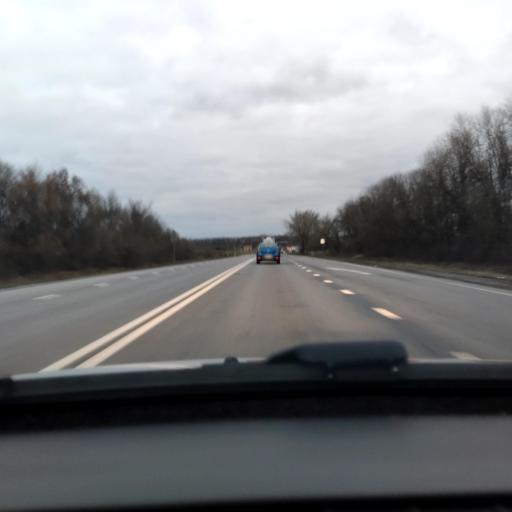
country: RU
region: Lipetsk
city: Borinskoye
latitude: 52.4211
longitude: 39.2555
